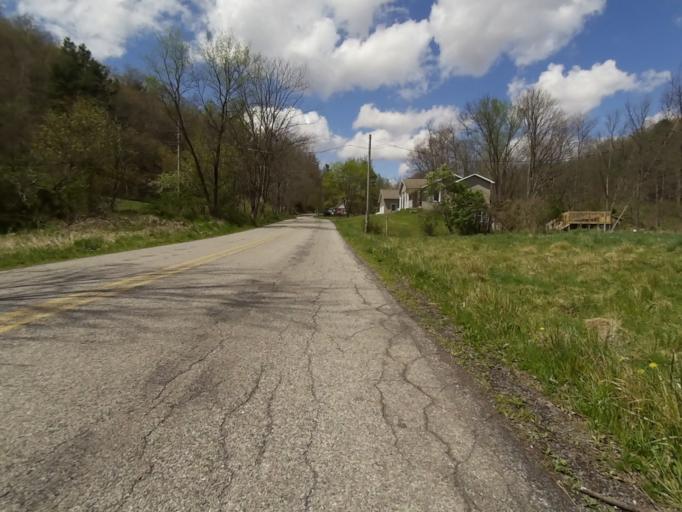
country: US
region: Pennsylvania
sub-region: Centre County
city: Milesburg
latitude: 40.9422
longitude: -77.8808
